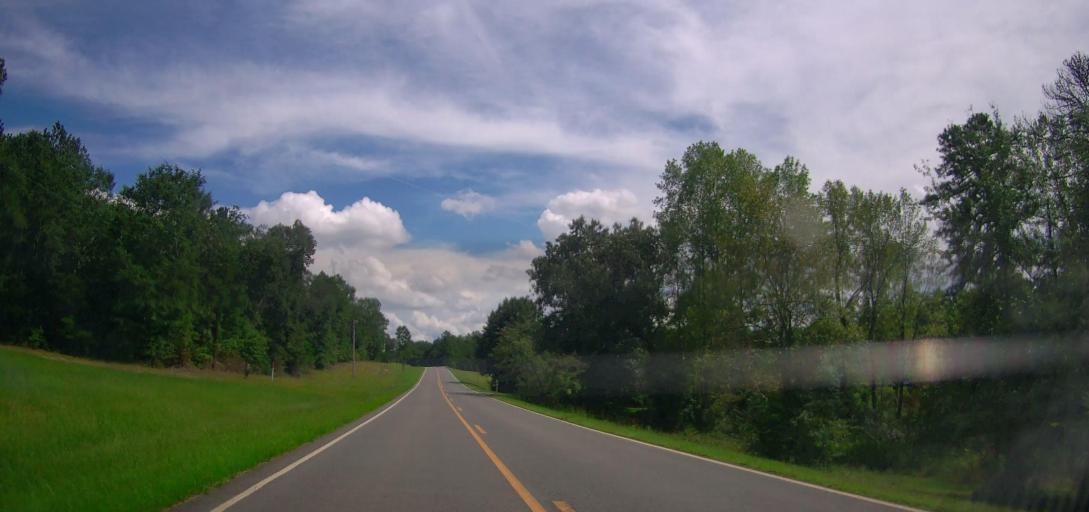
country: US
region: Georgia
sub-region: Taylor County
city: Butler
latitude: 32.5380
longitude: -84.2183
